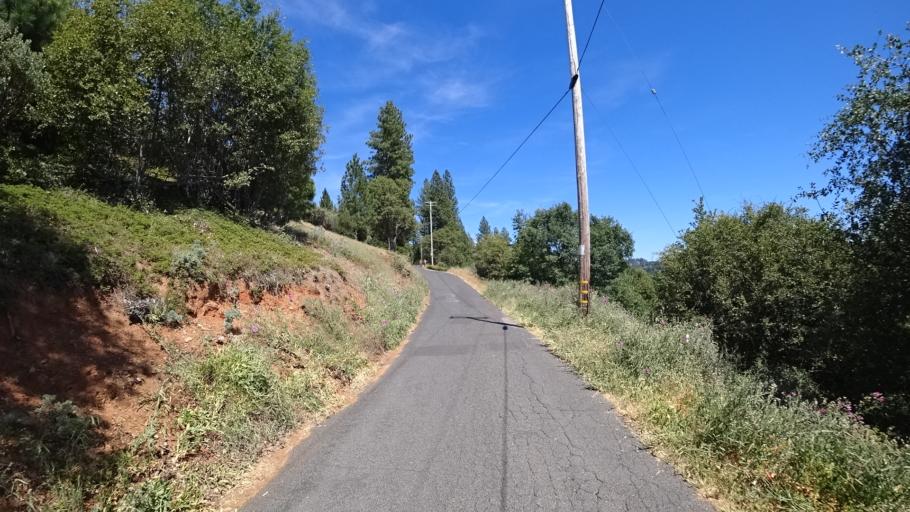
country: US
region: California
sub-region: Calaveras County
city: Forest Meadows
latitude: 38.1828
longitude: -120.4221
